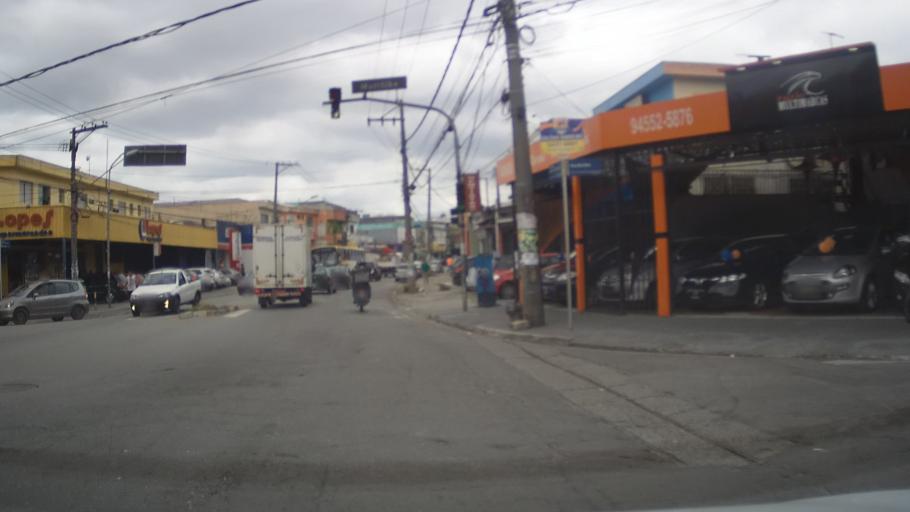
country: BR
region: Sao Paulo
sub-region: Itaquaquecetuba
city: Itaquaquecetuba
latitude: -23.4269
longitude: -46.4326
